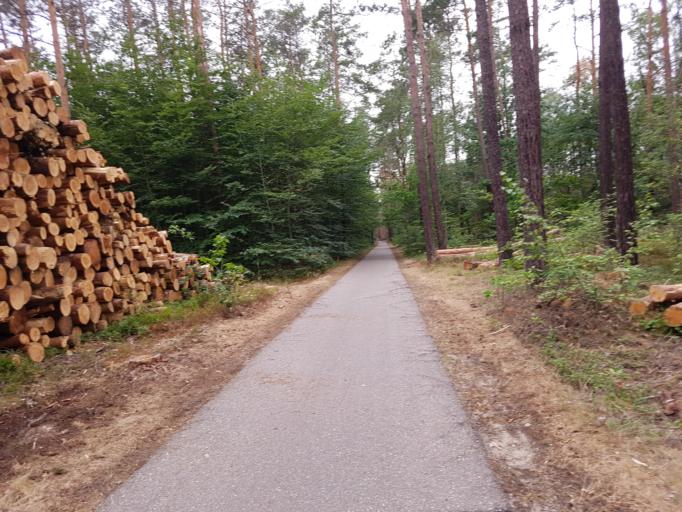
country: DE
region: Brandenburg
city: Finsterwalde
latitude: 51.6299
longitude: 13.6754
